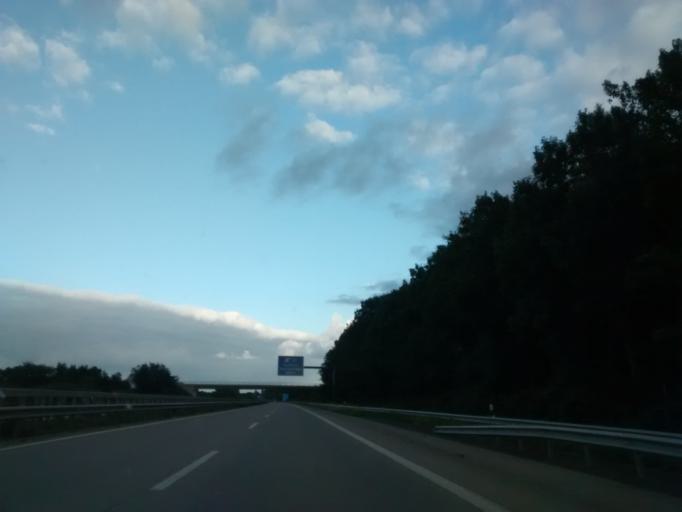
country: DE
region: Lower Saxony
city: Isterberg
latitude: 52.3366
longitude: 7.1273
